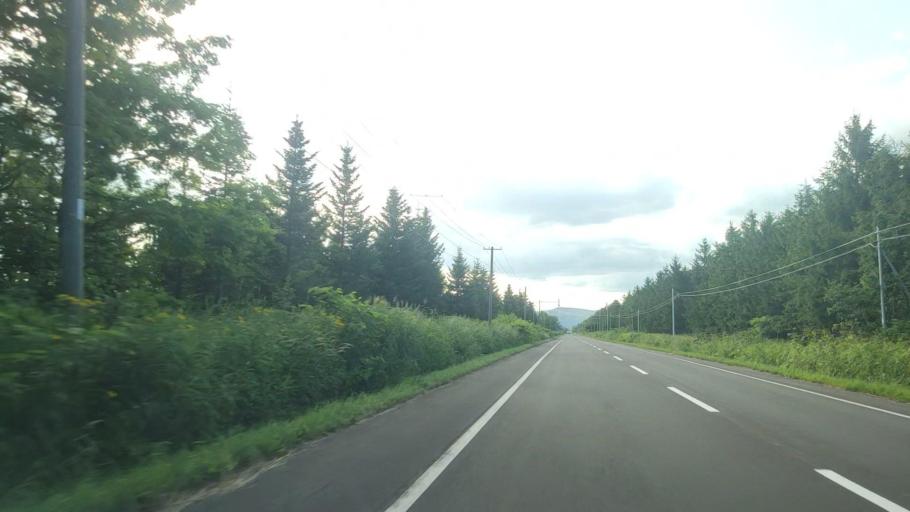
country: JP
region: Hokkaido
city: Makubetsu
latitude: 44.8838
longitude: 142.0144
